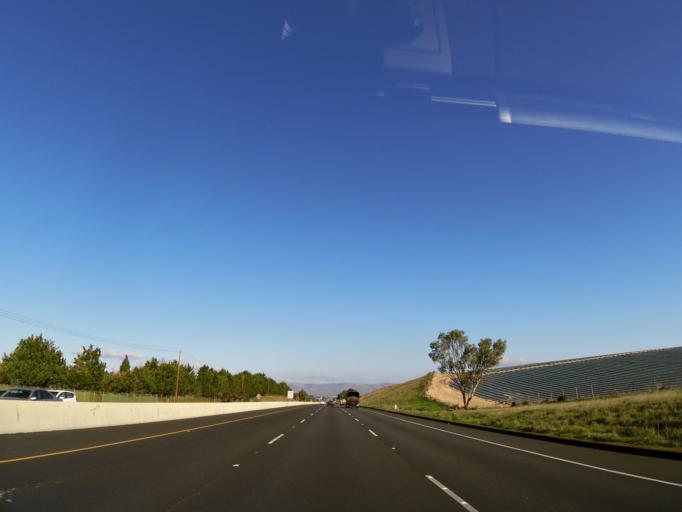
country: US
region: California
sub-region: Santa Barbara County
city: Orcutt
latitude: 34.8959
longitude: -120.4182
